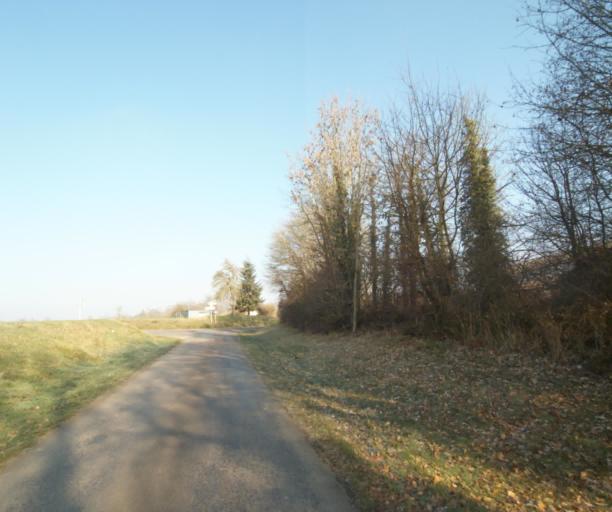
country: FR
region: Champagne-Ardenne
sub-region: Departement de la Haute-Marne
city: Wassy
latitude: 48.4719
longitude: 4.9650
